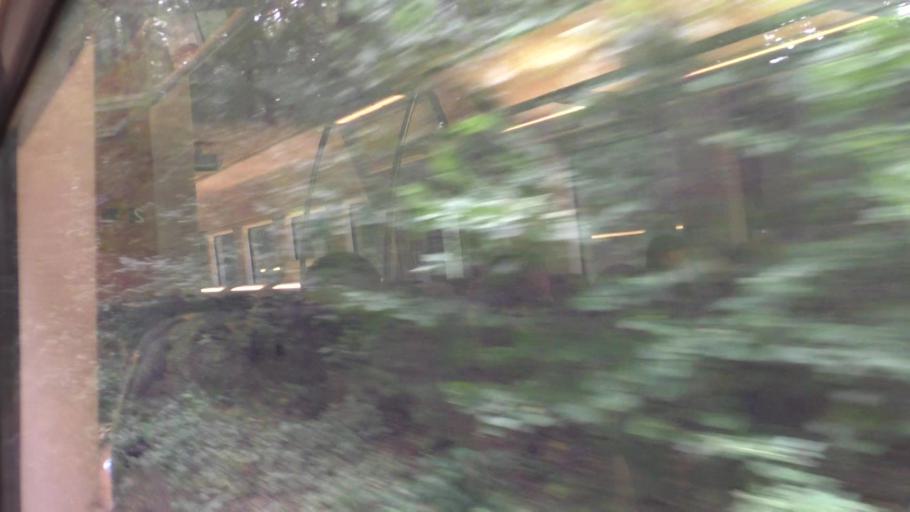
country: DE
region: Saxony
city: Goerlitz
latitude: 51.1534
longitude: 14.9543
